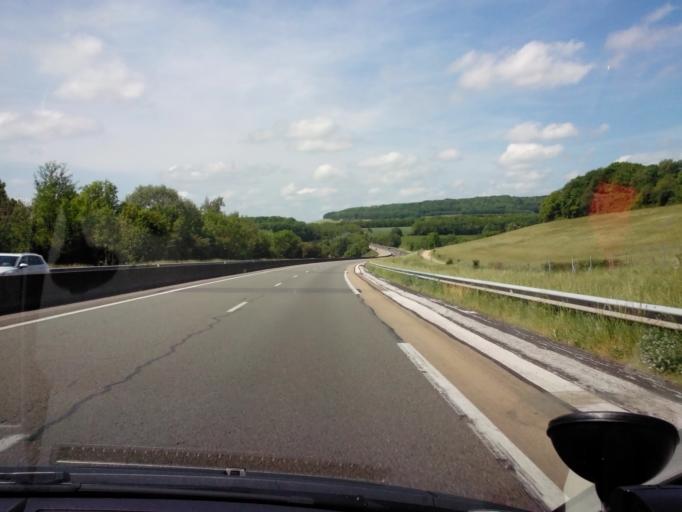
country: FR
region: Champagne-Ardenne
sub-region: Departement de la Haute-Marne
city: Avrecourt
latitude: 47.9599
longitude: 5.4595
